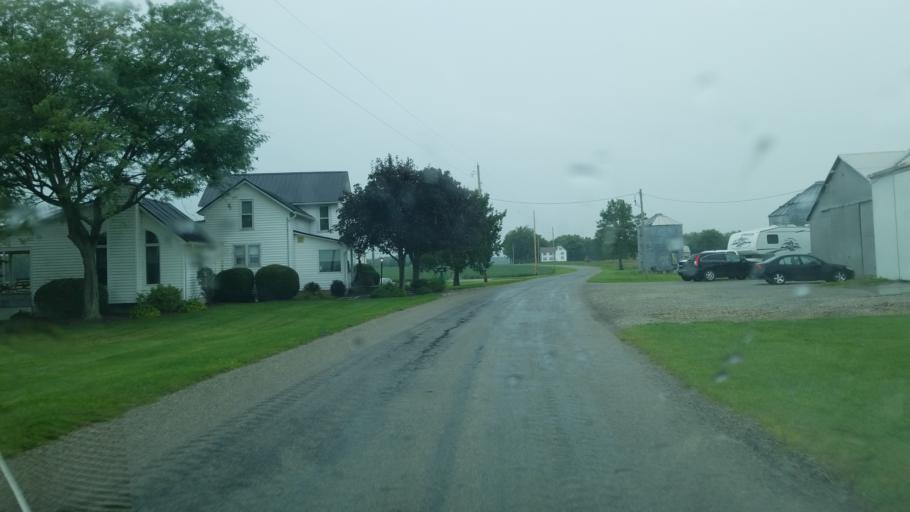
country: US
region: Ohio
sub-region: Huron County
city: Willard
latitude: 41.0166
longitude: -82.8129
